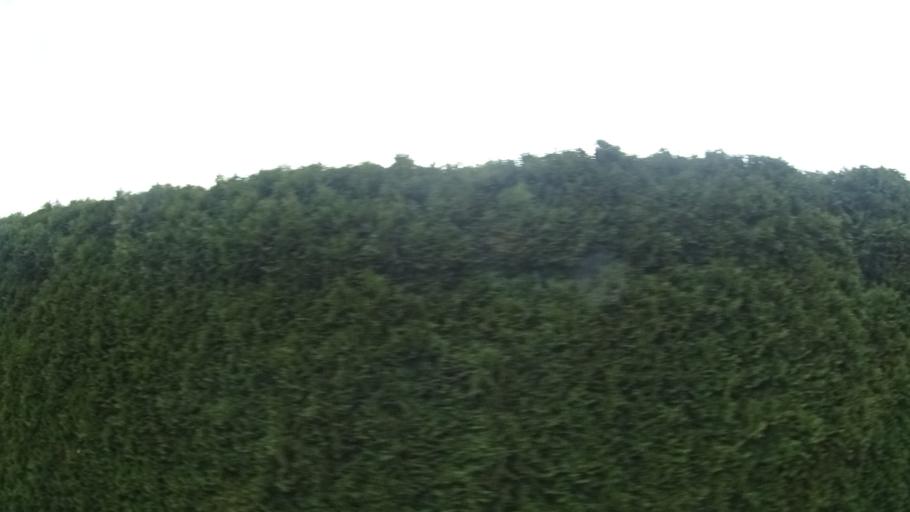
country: DE
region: Bavaria
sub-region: Regierungsbezirk Mittelfranken
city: Winkelhaid
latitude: 49.4125
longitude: 11.2966
